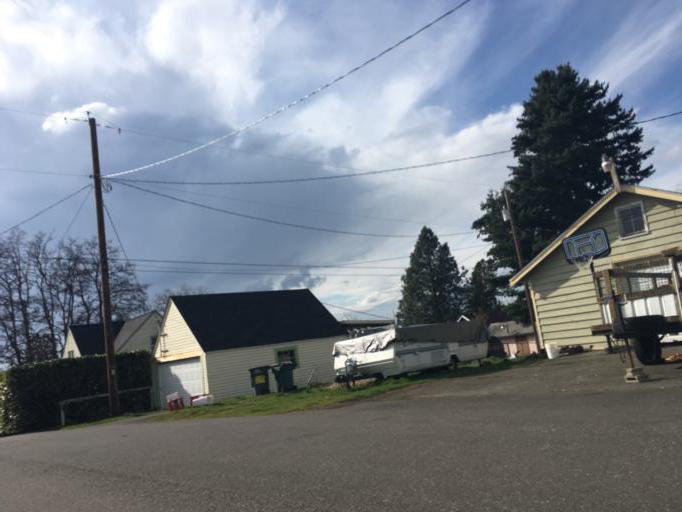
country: US
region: Washington
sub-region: Whatcom County
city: Bellingham
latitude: 48.7519
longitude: -122.4667
